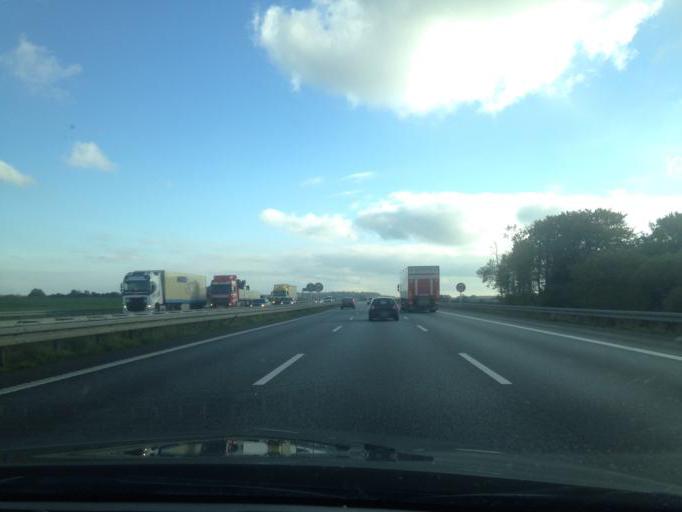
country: DK
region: South Denmark
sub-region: Vejle Kommune
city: Borkop
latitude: 55.6278
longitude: 9.5670
